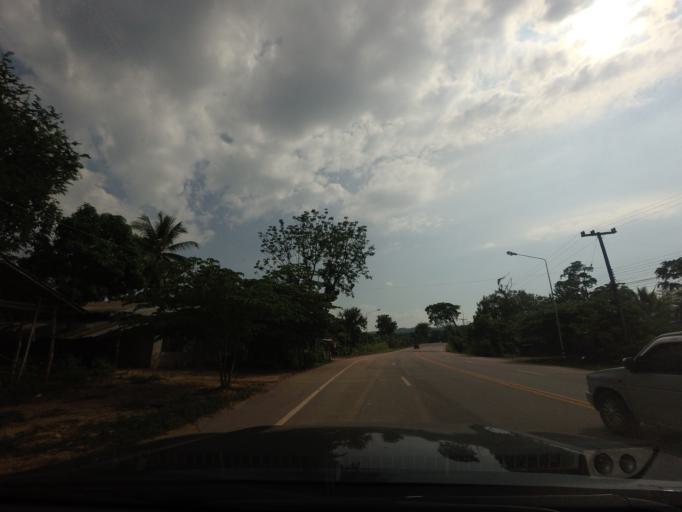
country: TH
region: Phitsanulok
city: Nakhon Thai
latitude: 17.0322
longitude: 100.9139
